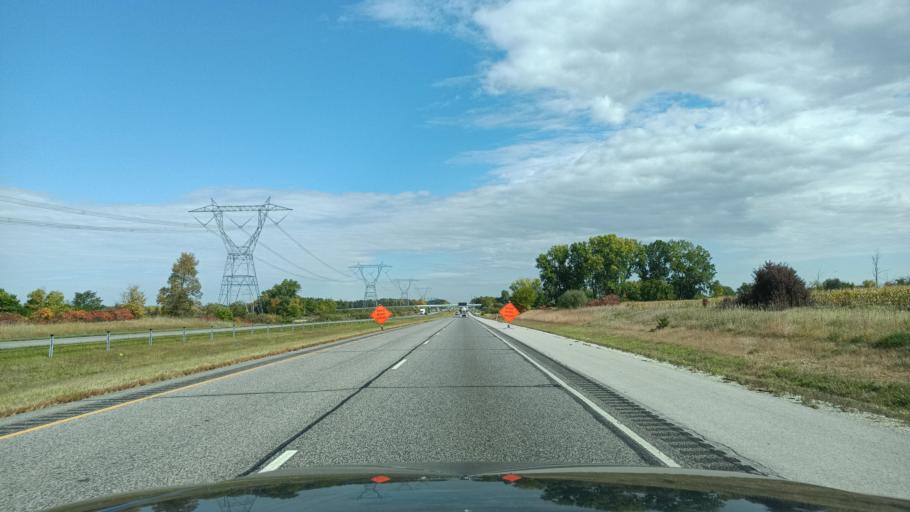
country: US
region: Indiana
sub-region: Huntington County
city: Roanoke
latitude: 40.9260
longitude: -85.3178
